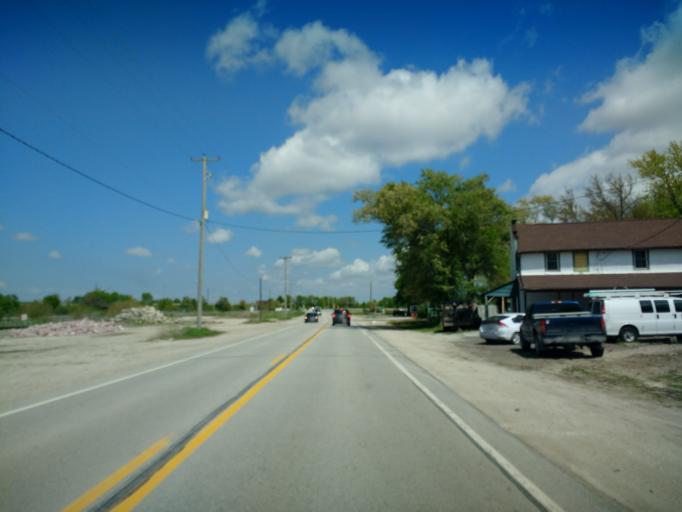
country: US
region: Iowa
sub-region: Harrison County
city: Missouri Valley
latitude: 41.4961
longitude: -95.8919
